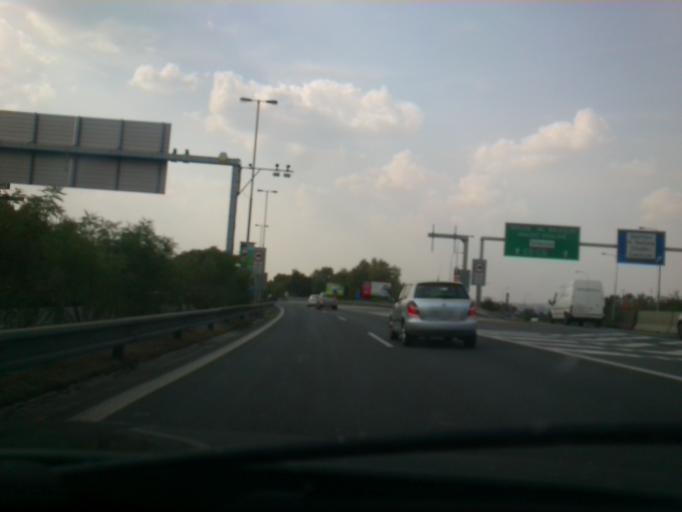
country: CZ
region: Central Bohemia
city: Vestec
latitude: 50.0378
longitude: 14.4896
